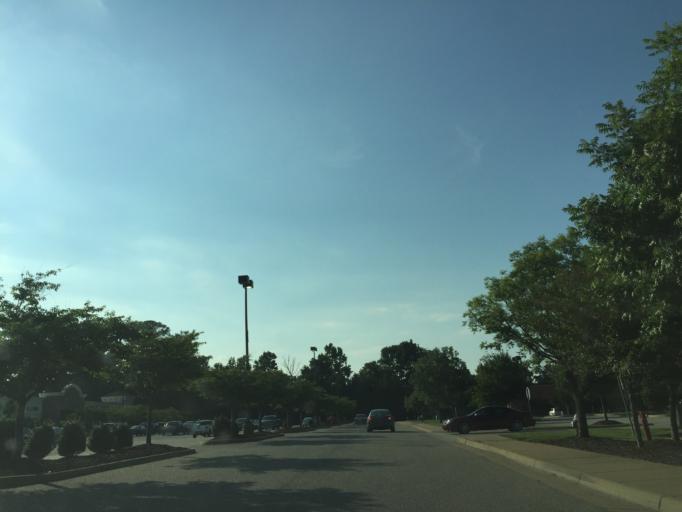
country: US
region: Virginia
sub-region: York County
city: Yorktown
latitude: 37.1308
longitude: -76.5152
